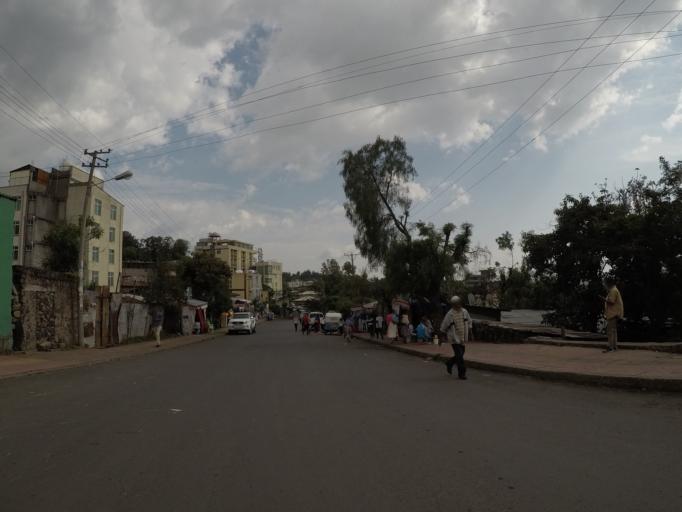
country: ET
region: Amhara
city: Gondar
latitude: 12.6153
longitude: 37.4697
